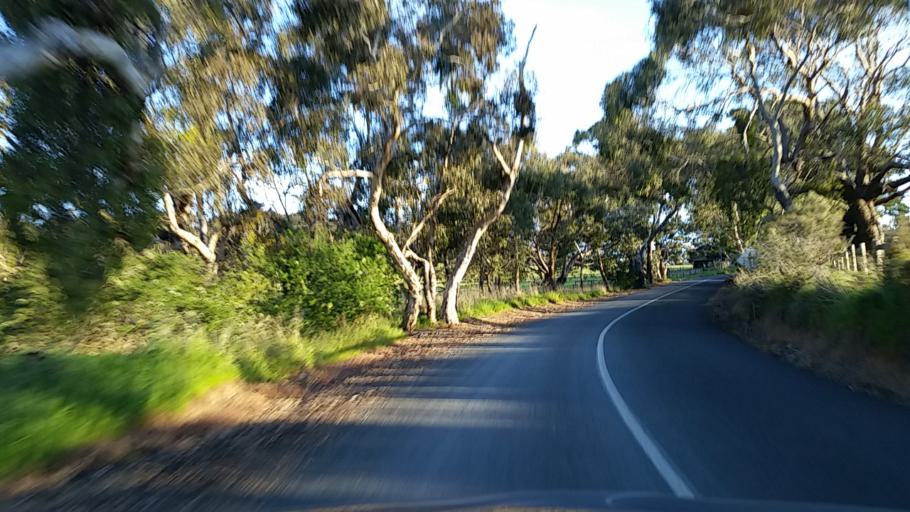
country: AU
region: South Australia
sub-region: Alexandrina
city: Mount Compass
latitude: -35.3224
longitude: 138.6682
